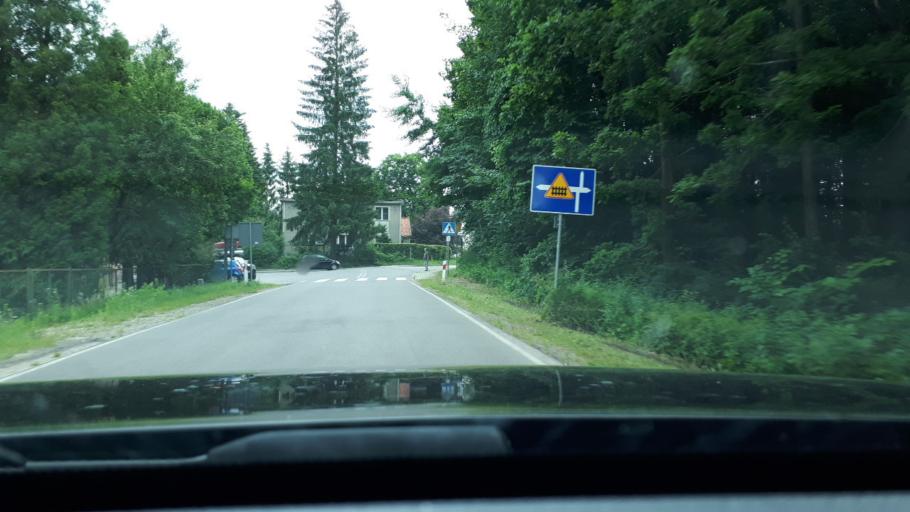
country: PL
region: Warmian-Masurian Voivodeship
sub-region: Powiat ostrodzki
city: Ostroda
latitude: 53.6909
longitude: 20.0928
